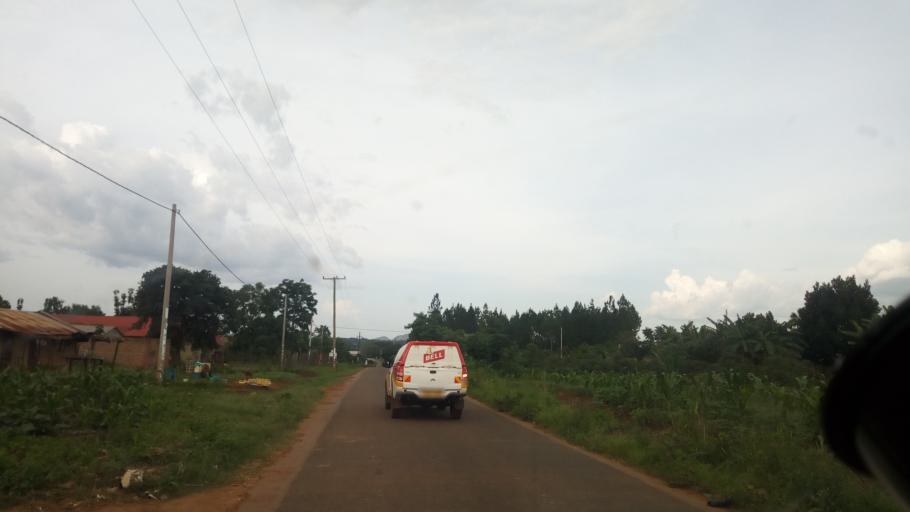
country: UG
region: Northern Region
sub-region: Lira District
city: Lira
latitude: 2.2571
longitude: 32.8507
